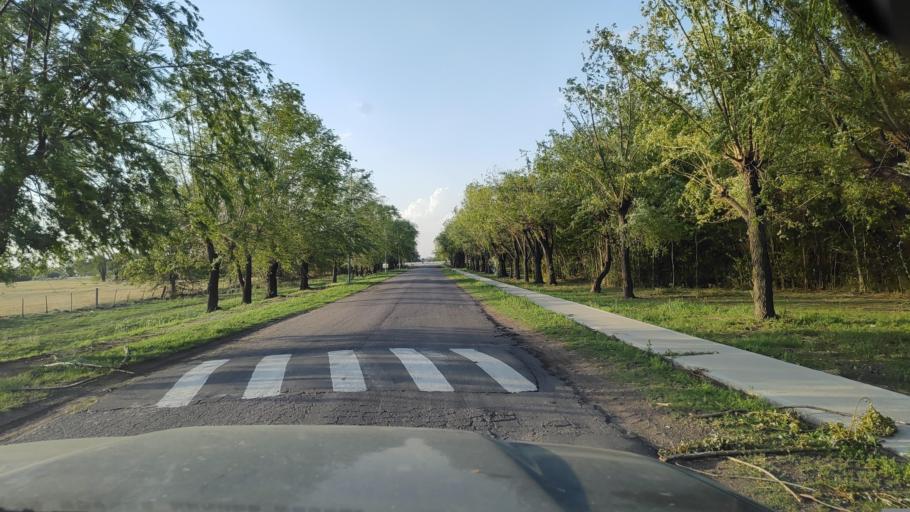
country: AR
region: Buenos Aires
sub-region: Partido de Lujan
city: Lujan
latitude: -34.5482
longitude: -59.2104
